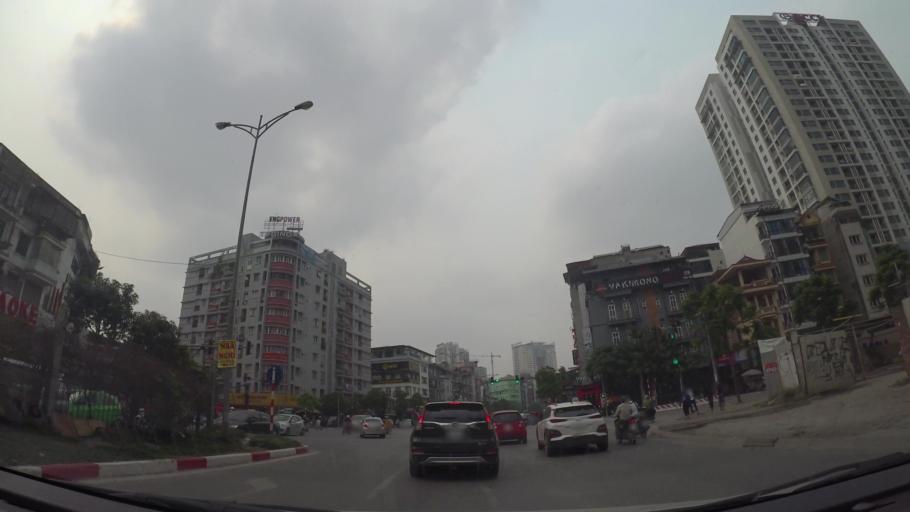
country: VN
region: Ha Noi
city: Cau Dien
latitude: 21.0298
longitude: 105.7757
